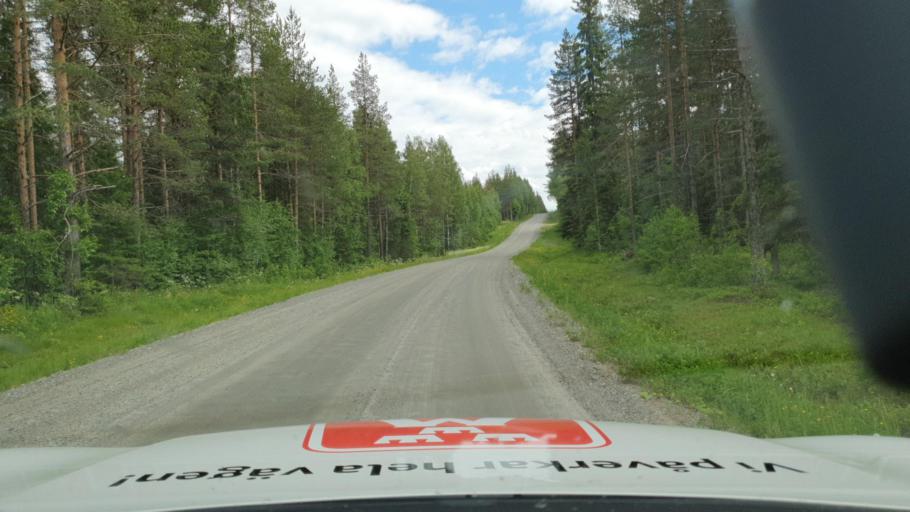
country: SE
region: Vaesterbotten
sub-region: Norsjo Kommun
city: Norsjoe
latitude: 64.8014
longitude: 19.6344
